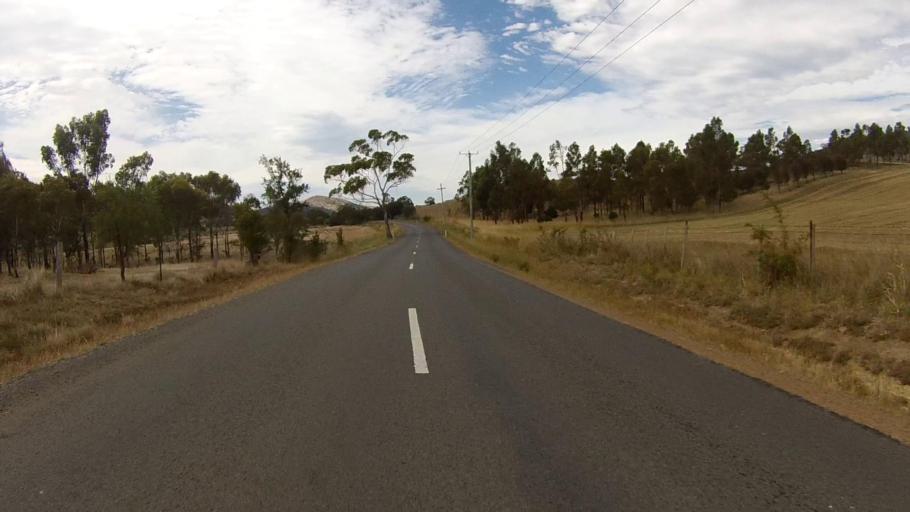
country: AU
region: Tasmania
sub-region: Brighton
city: Old Beach
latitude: -42.7164
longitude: 147.3849
